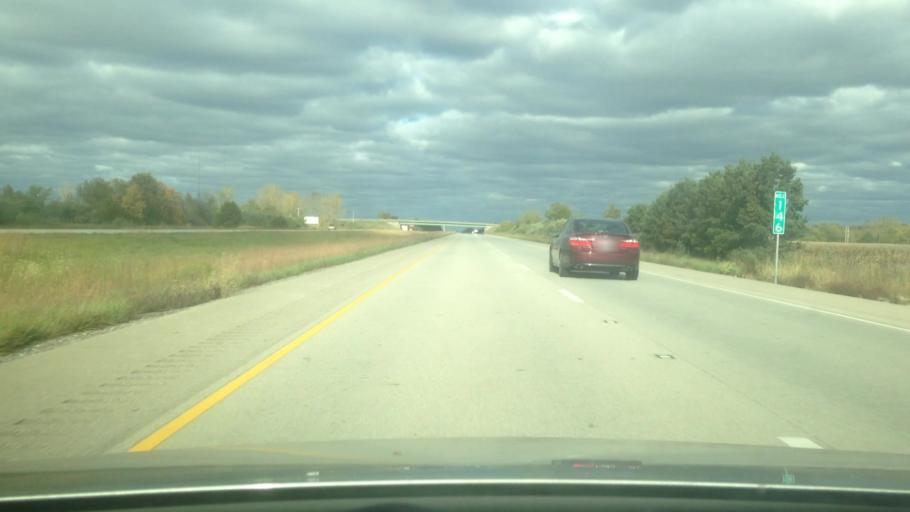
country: US
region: Illinois
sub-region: Macon County
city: Forsyth
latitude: 39.9153
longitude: -88.8655
